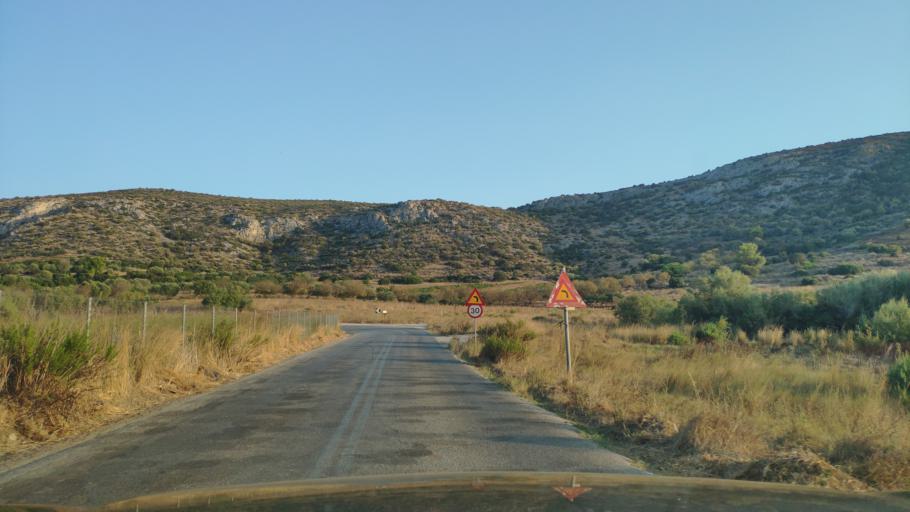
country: GR
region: Attica
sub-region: Nomarchia Anatolikis Attikis
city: Limin Mesoyaias
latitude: 37.9225
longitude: 23.9942
